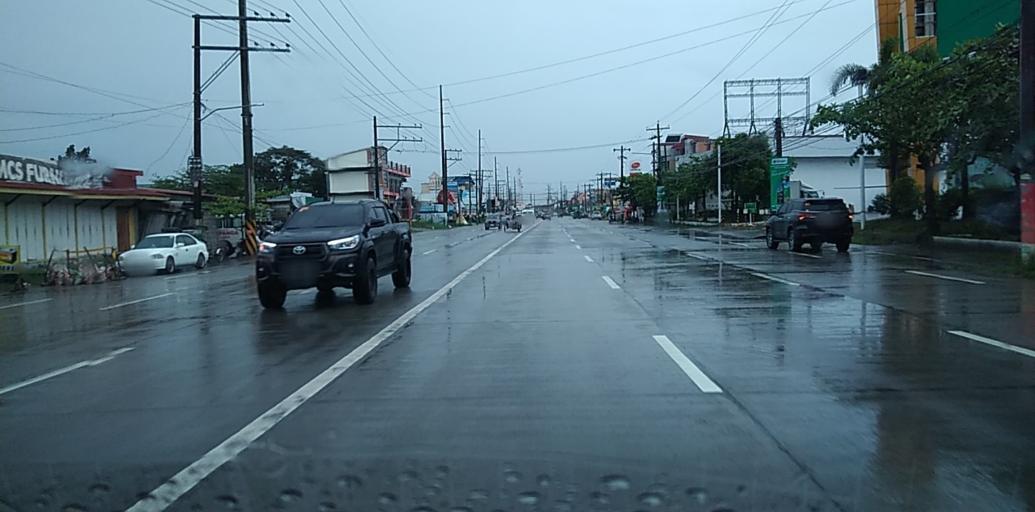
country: PH
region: Central Luzon
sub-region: Province of Pampanga
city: Del Pilar
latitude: 15.0518
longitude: 120.7051
